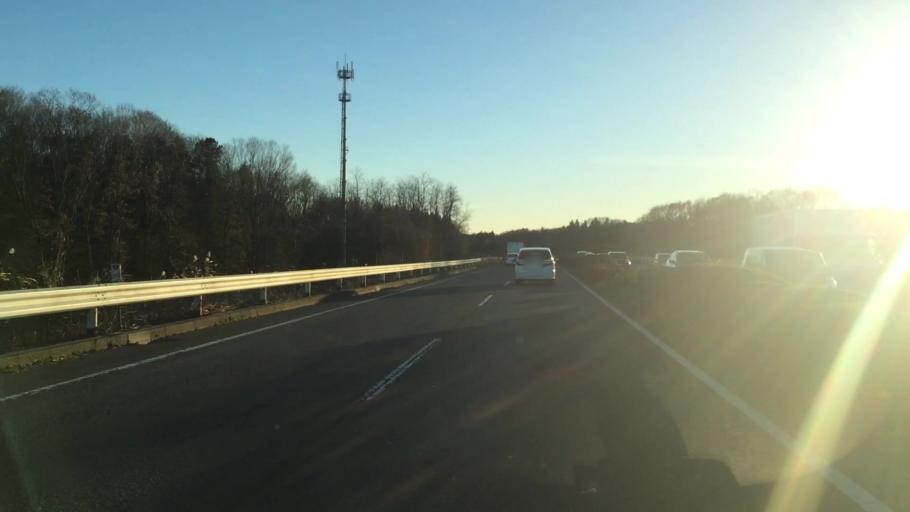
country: JP
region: Tochigi
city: Utsunomiya-shi
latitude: 36.5235
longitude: 139.9216
